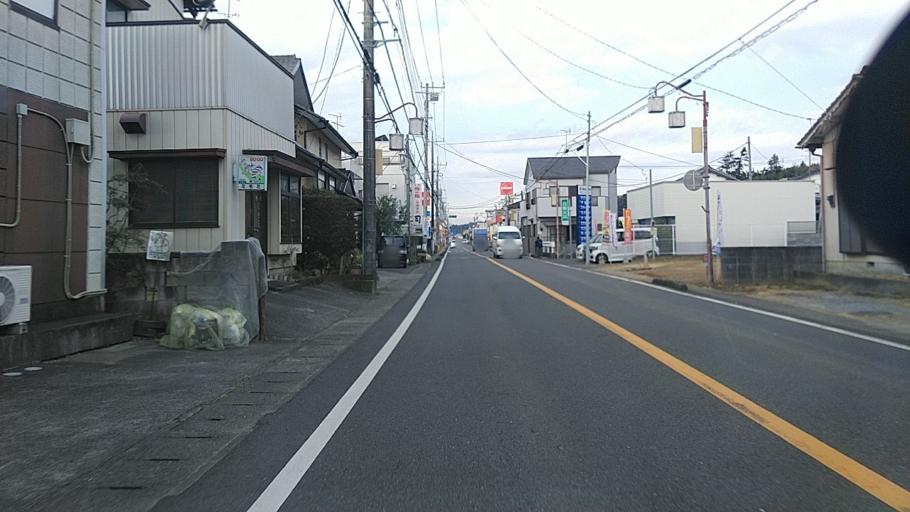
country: JP
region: Chiba
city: Togane
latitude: 35.5586
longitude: 140.3499
